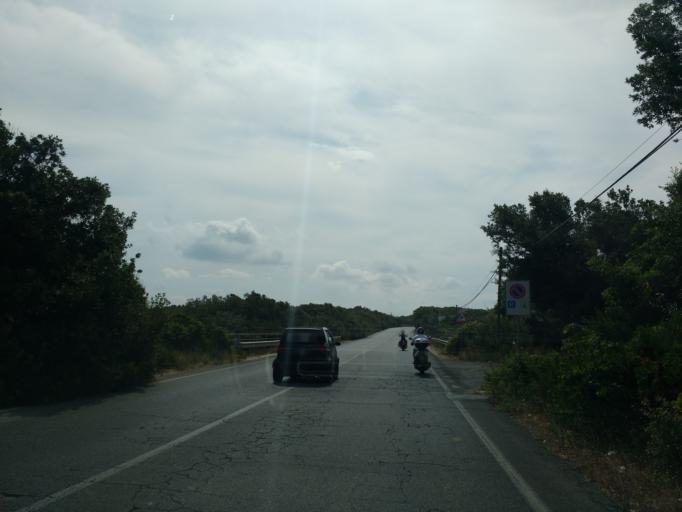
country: IT
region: Latium
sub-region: Citta metropolitana di Roma Capitale
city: Torvaianica
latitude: 41.6863
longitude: 12.3757
